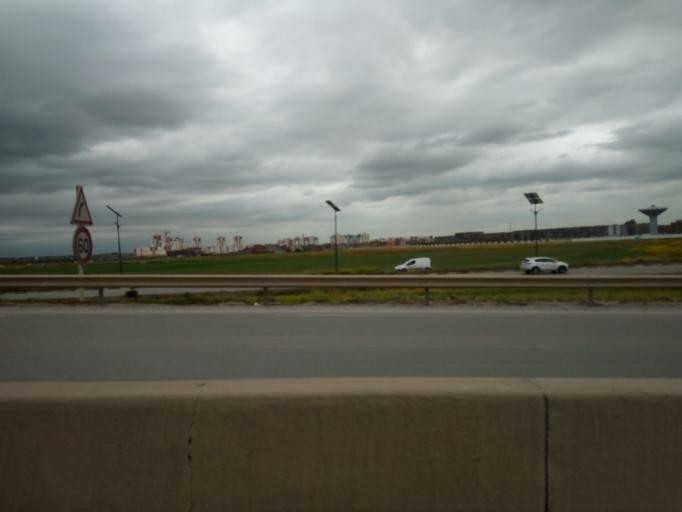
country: DZ
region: Setif
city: El Eulma
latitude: 36.1747
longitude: 5.6740
